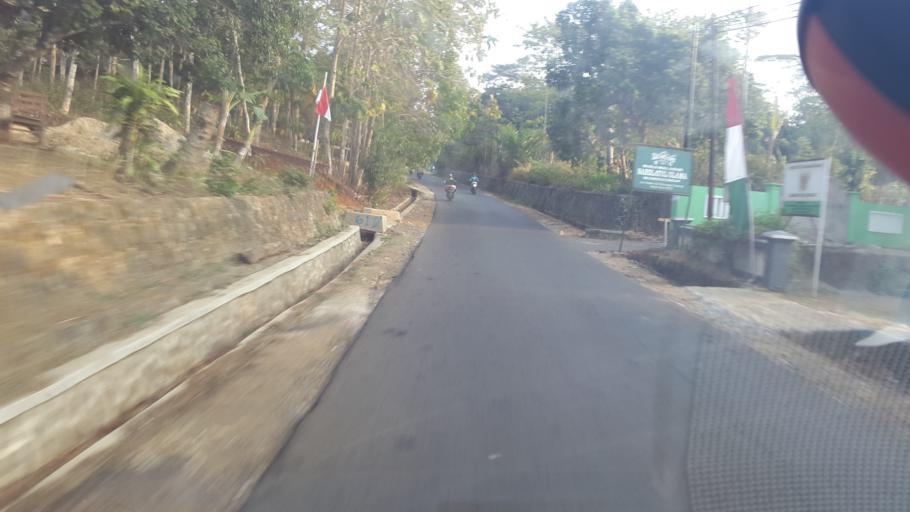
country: ID
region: West Java
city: Ciracap
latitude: -7.3384
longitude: 106.5264
